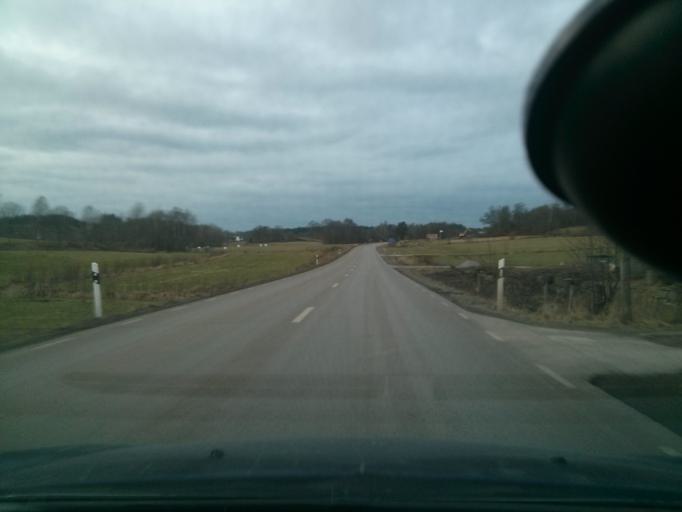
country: SE
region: Blekinge
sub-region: Ronneby Kommun
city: Brakne-Hoby
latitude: 56.2980
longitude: 15.1968
